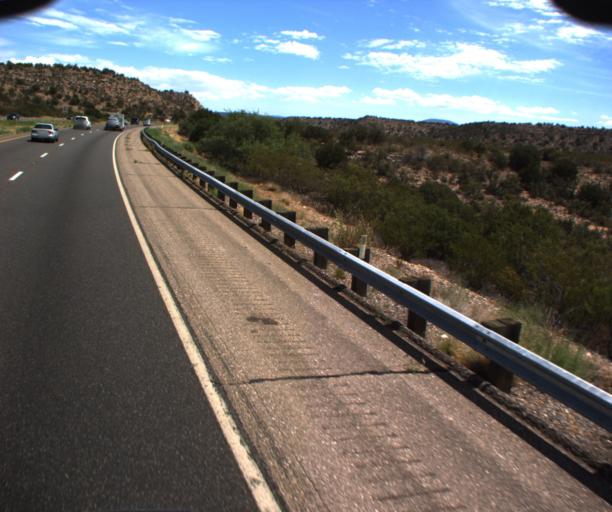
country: US
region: Arizona
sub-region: Yavapai County
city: Lake Montezuma
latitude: 34.6577
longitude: -111.7921
